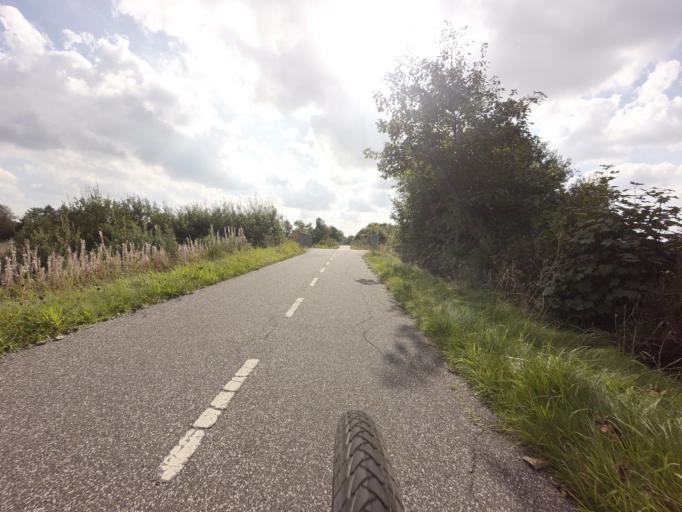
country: DK
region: Central Jutland
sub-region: Herning Kommune
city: Sunds
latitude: 56.1808
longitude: 9.0058
